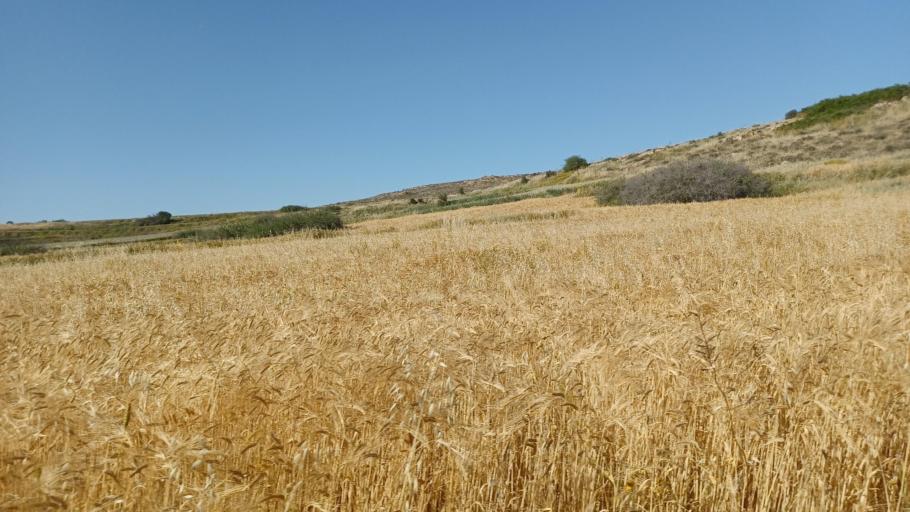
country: CY
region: Lefkosia
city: Mammari
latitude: 35.1626
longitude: 33.2391
